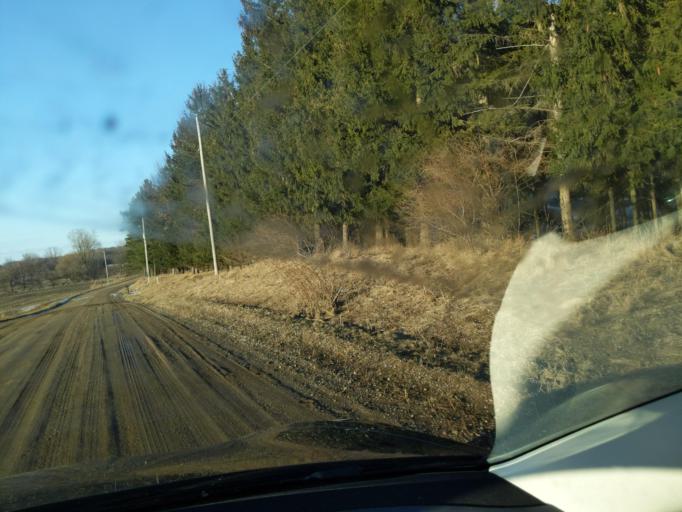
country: US
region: Michigan
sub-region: Ingham County
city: Stockbridge
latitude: 42.5427
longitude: -84.2880
